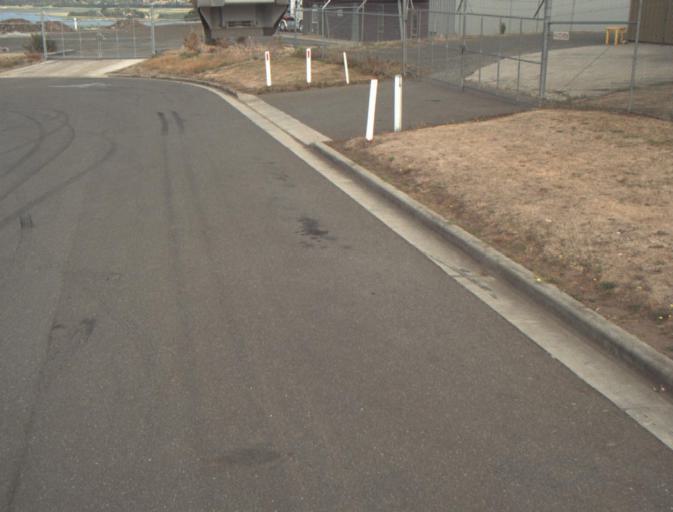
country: AU
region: Tasmania
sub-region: Launceston
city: Mayfield
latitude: -41.3741
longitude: 147.1148
